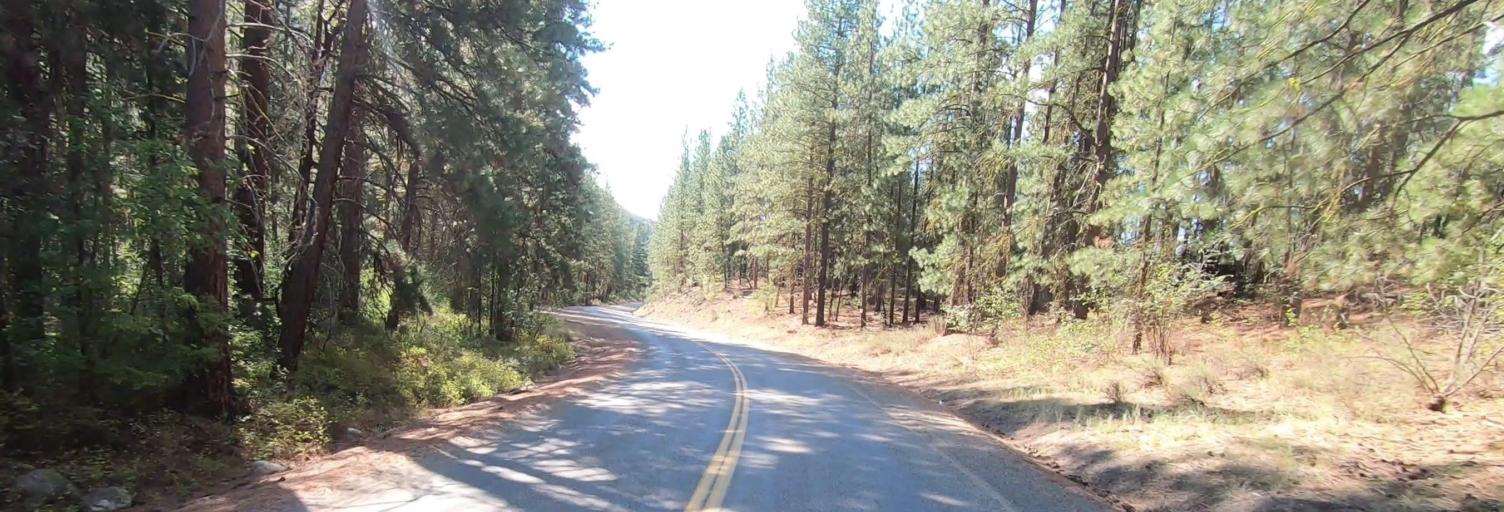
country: US
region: Washington
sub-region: Okanogan County
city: Brewster
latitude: 48.5410
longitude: -120.1795
